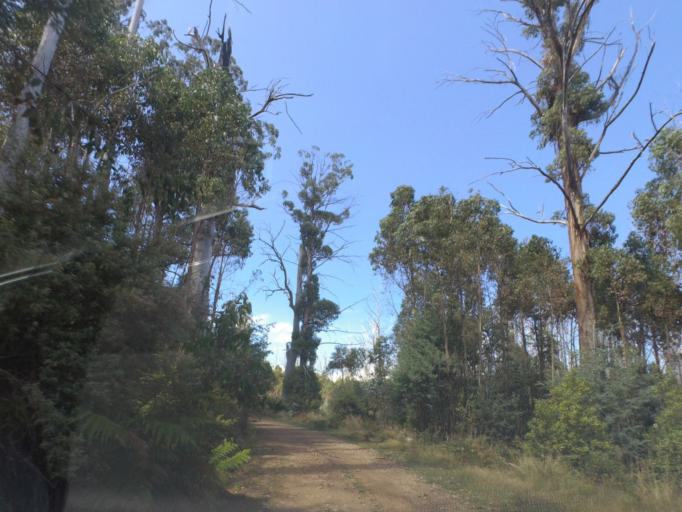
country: AU
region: Victoria
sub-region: Murrindindi
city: Alexandra
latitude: -37.4801
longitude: 145.8380
